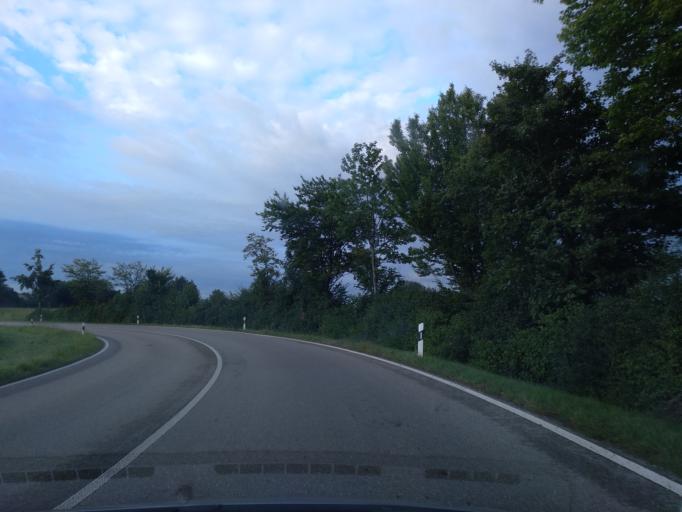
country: DE
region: Bavaria
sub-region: Upper Bavaria
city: Burgheim
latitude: 48.7113
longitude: 11.0067
